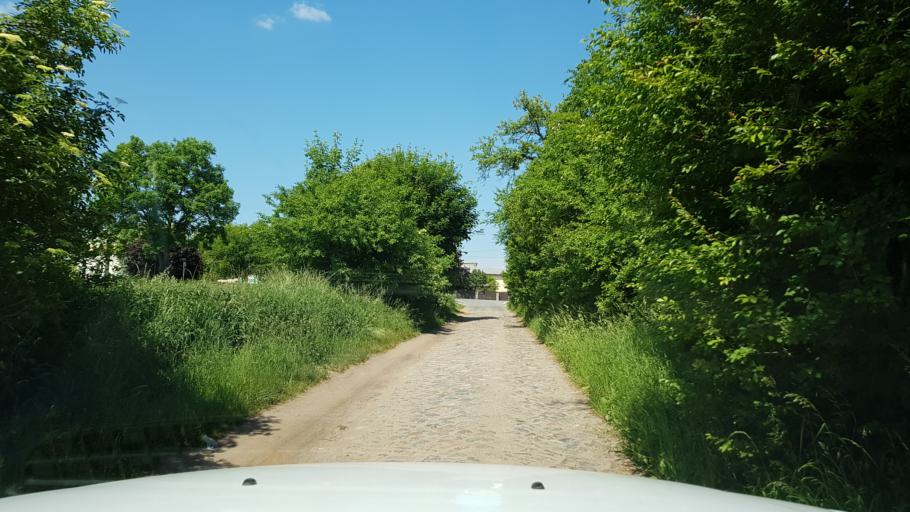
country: PL
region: West Pomeranian Voivodeship
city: Trzcinsko Zdroj
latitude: 52.9615
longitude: 14.5915
